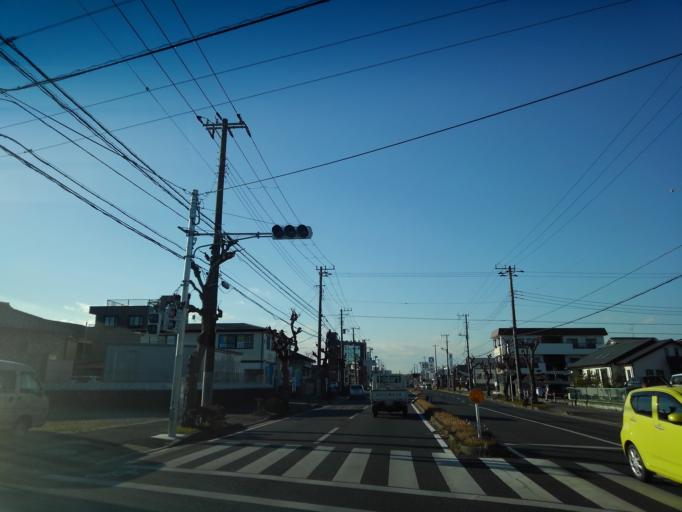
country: JP
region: Chiba
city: Kimitsu
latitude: 35.3301
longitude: 139.8949
